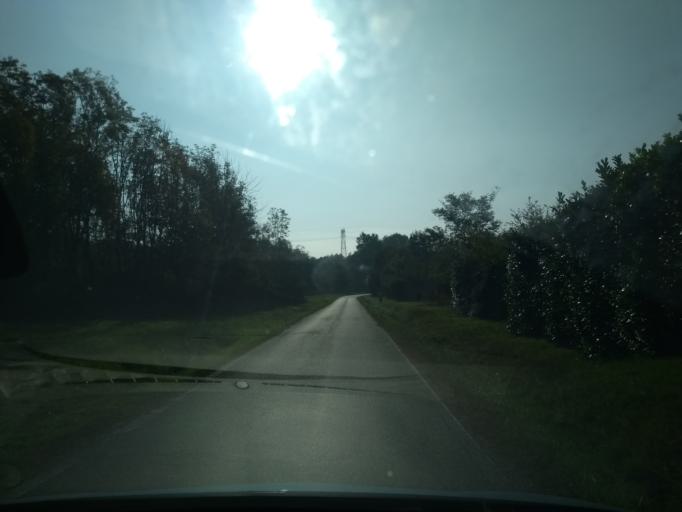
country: IT
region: Piedmont
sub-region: Provincia di Torino
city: Vallo Torinese
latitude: 45.2206
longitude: 7.5058
